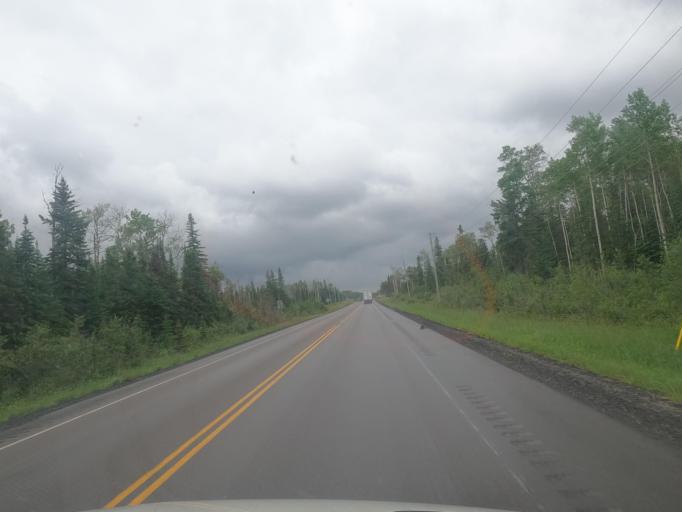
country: CA
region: Ontario
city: Greenstone
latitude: 49.7832
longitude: -86.5782
